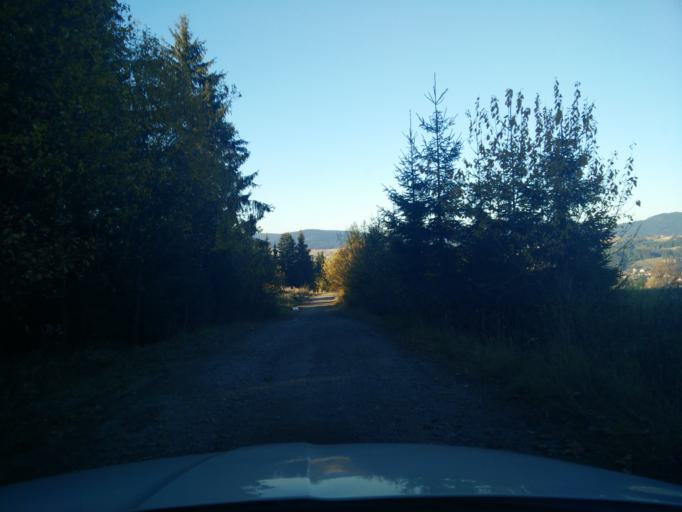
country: SK
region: Zilinsky
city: Oravska Lesna
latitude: 49.3541
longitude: 19.1537
